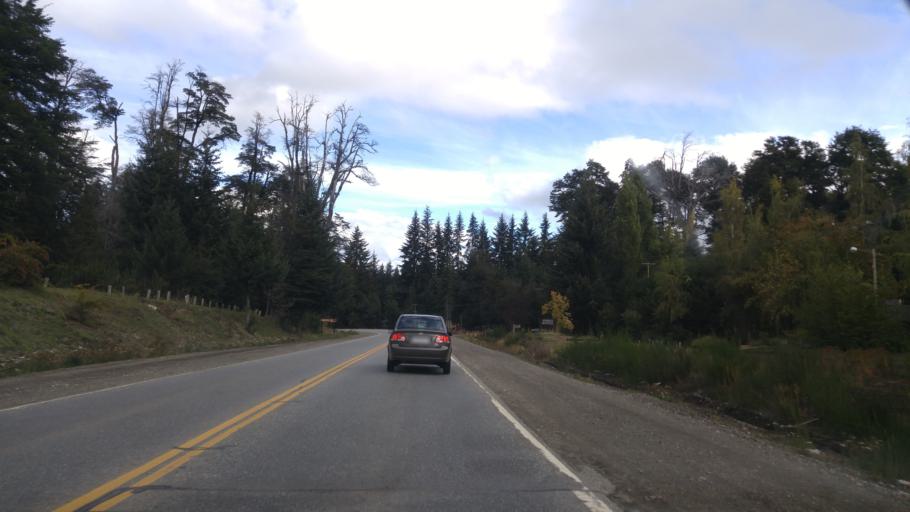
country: AR
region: Neuquen
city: Villa La Angostura
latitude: -40.7914
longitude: -71.5954
